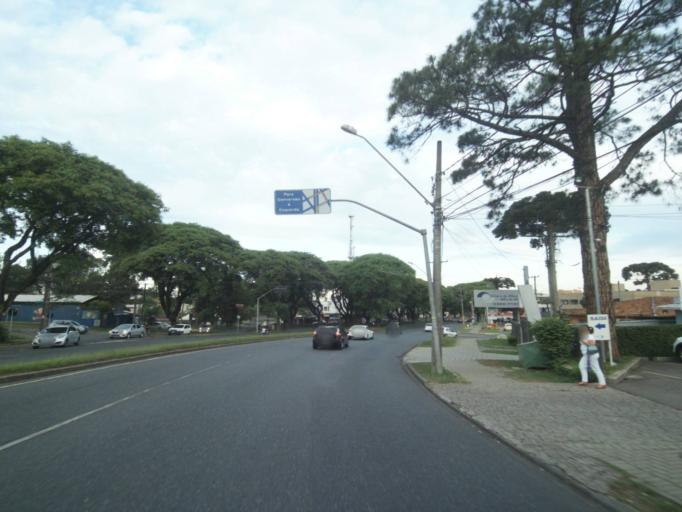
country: BR
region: Parana
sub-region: Curitiba
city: Curitiba
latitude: -25.4275
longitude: -49.2400
